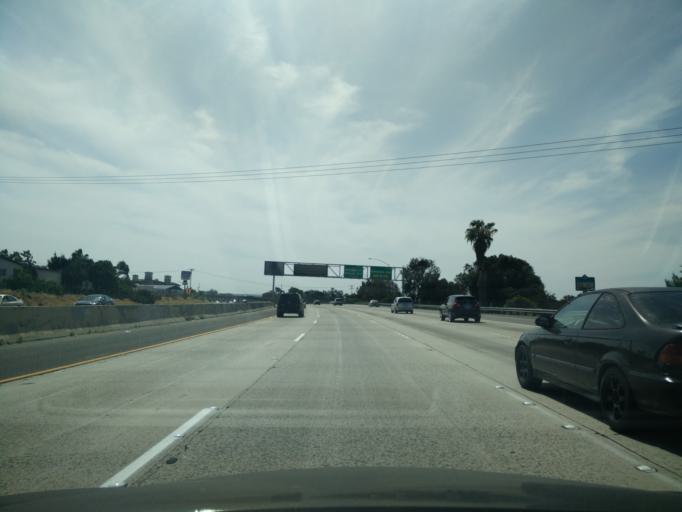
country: US
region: California
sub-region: San Diego County
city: Imperial Beach
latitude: 32.5806
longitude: -117.0864
